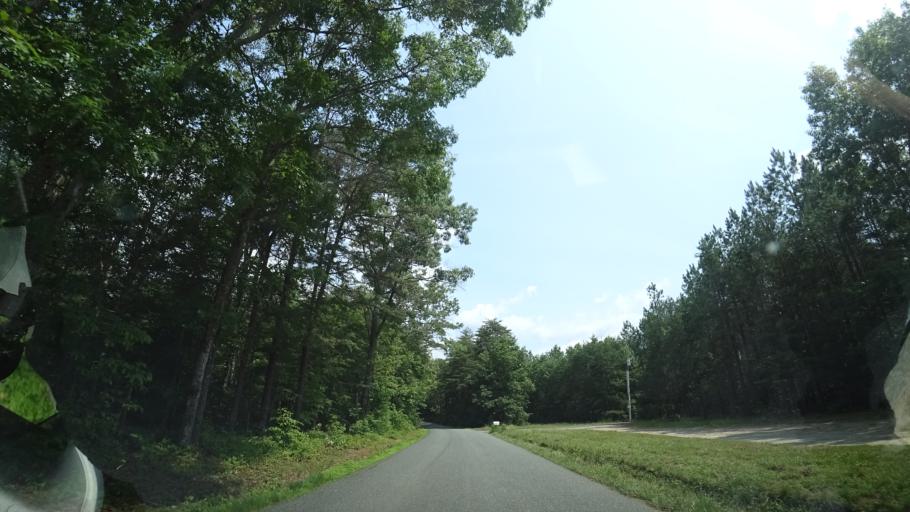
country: US
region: Virginia
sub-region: Louisa County
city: Louisa
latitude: 38.1064
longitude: -77.7956
